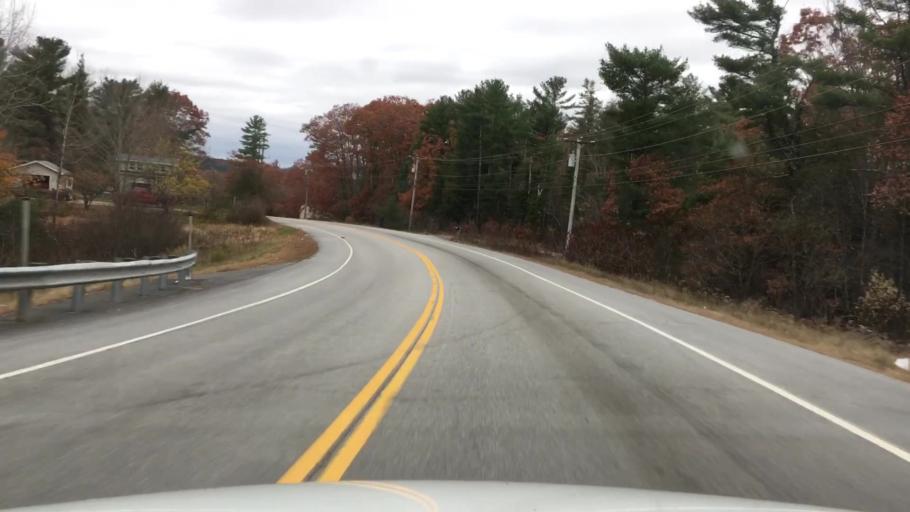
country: US
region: Maine
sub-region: Hancock County
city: Orland
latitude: 44.5572
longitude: -68.6983
